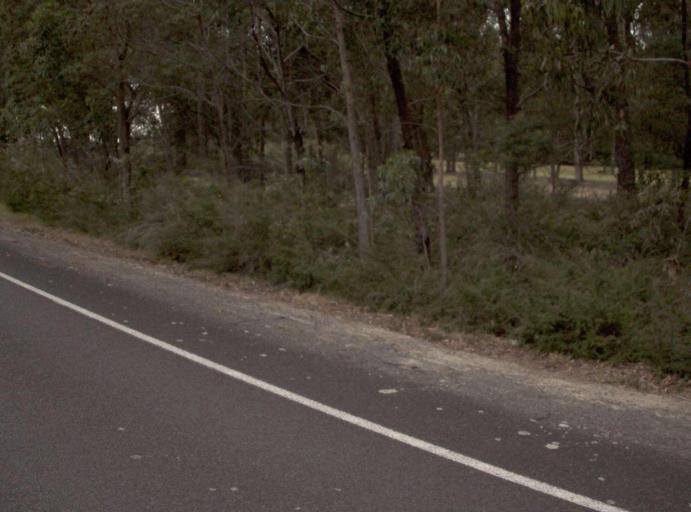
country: AU
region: Victoria
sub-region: Wellington
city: Sale
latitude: -38.3496
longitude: 146.9989
